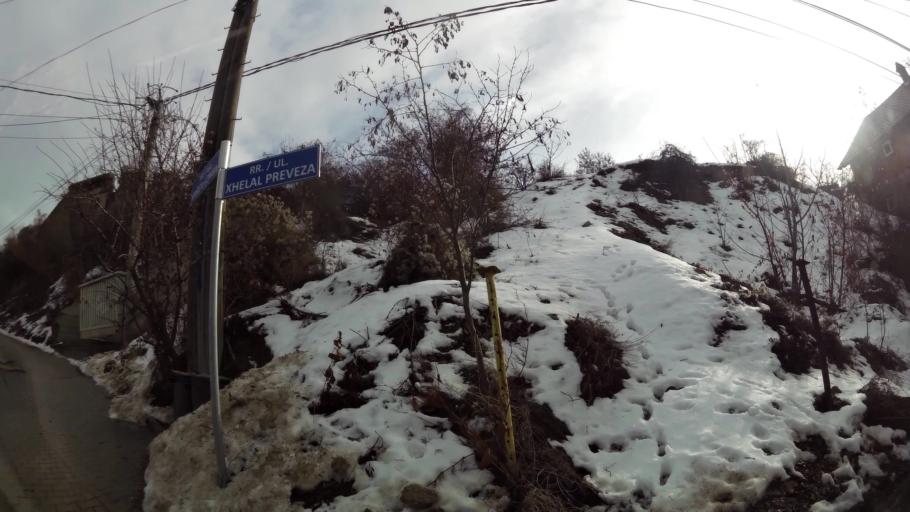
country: XK
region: Pristina
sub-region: Komuna e Prishtines
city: Pristina
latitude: 42.6744
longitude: 21.1761
